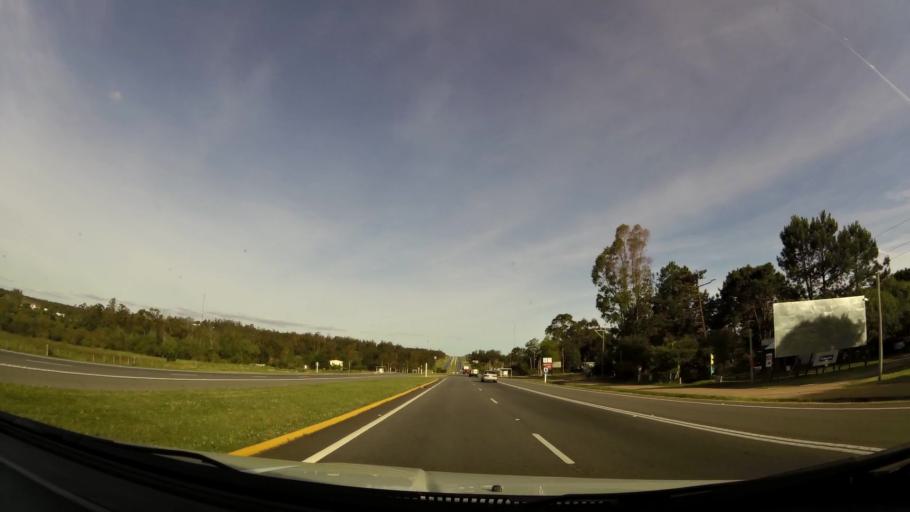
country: UY
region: Canelones
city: La Floresta
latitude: -34.7768
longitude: -55.5628
